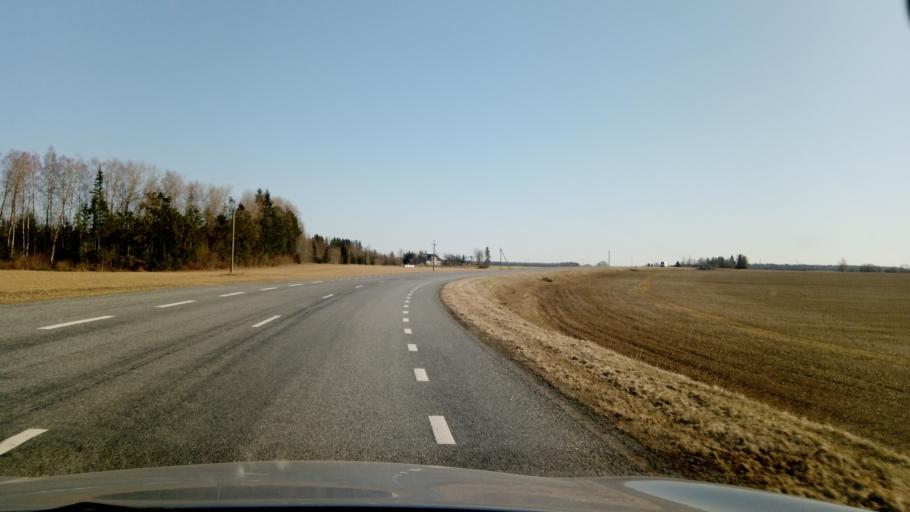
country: EE
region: Jaervamaa
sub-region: Jaerva-Jaani vald
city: Jarva-Jaani
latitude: 59.0687
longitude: 25.9339
